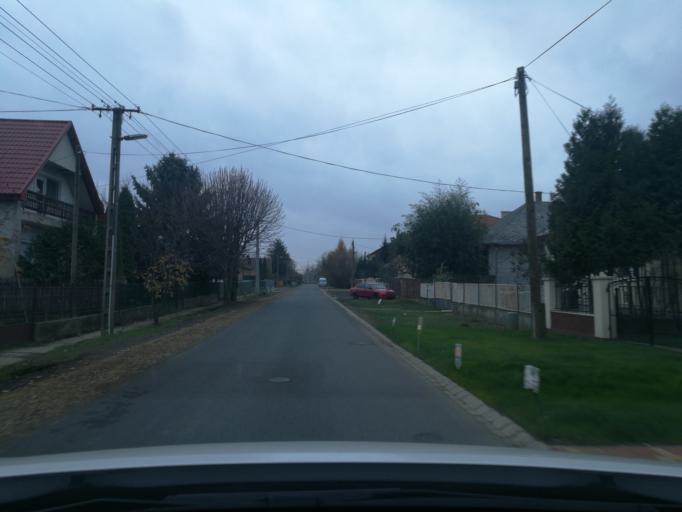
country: HU
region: Szabolcs-Szatmar-Bereg
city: Nyirpazony
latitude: 47.9519
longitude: 21.7823
